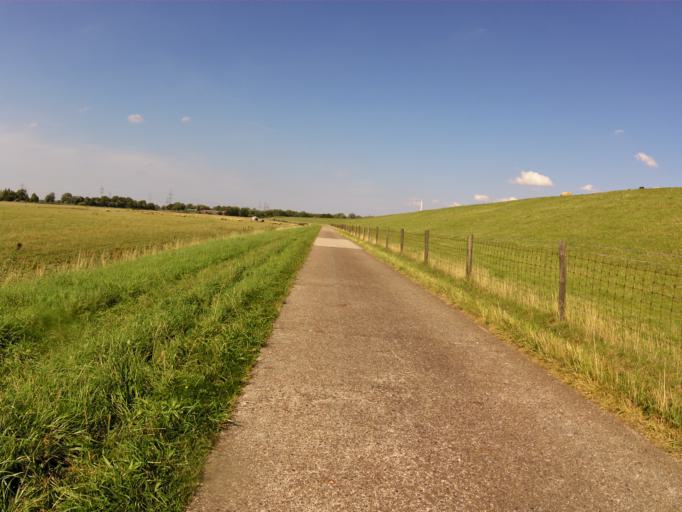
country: DE
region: Lower Saxony
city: Nordenham
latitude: 53.4169
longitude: 8.4722
